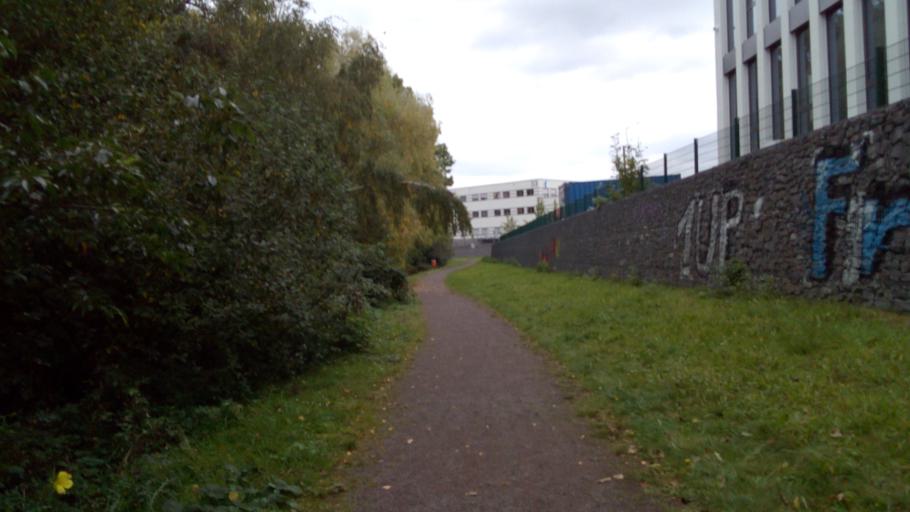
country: DE
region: North Rhine-Westphalia
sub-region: Regierungsbezirk Arnsberg
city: Bochum
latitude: 51.4453
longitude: 7.2474
